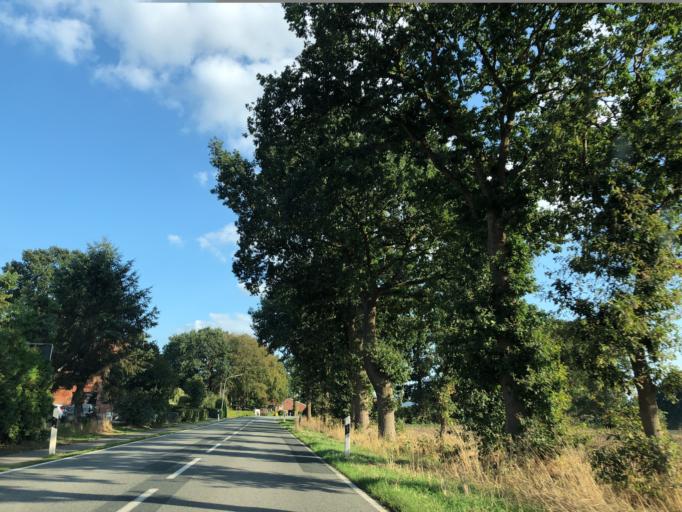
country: DE
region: Lower Saxony
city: Rhede
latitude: 53.0083
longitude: 7.2291
